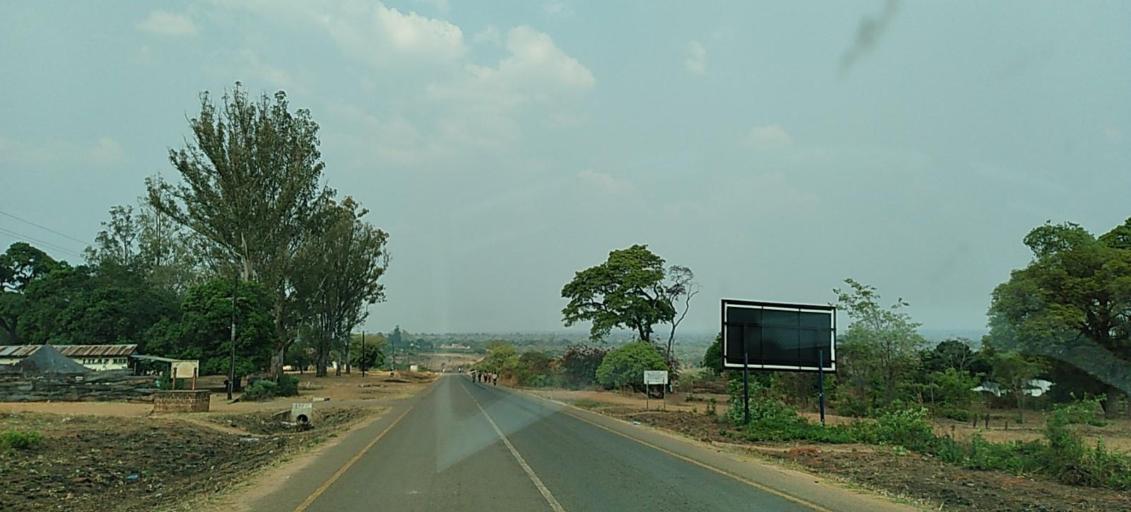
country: ZM
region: North-Western
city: Kabompo
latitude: -13.5920
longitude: 24.2092
